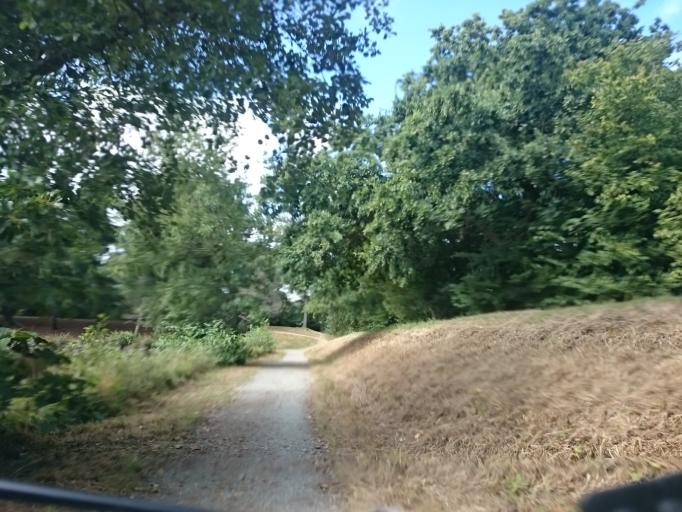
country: FR
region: Brittany
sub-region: Departement d'Ille-et-Vilaine
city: Cesson-Sevigne
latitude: 48.1269
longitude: -1.5892
